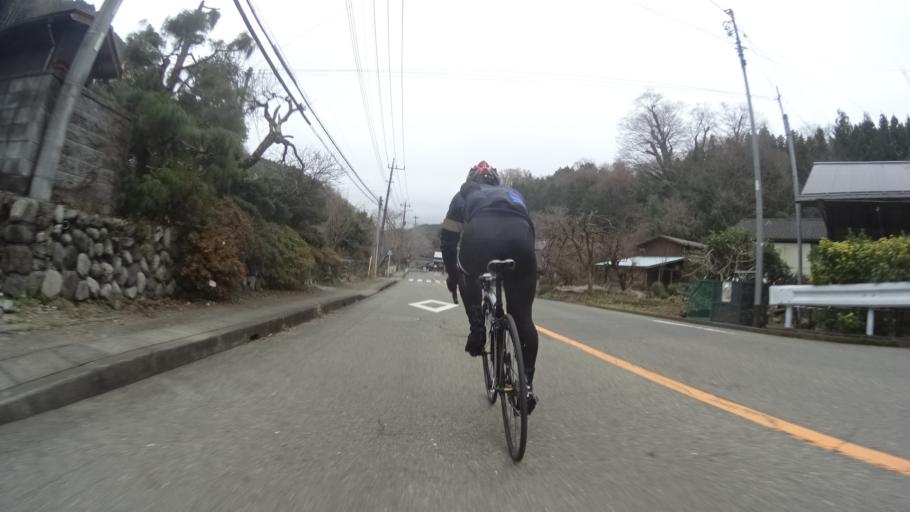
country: JP
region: Yamanashi
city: Uenohara
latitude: 35.6269
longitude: 139.1487
